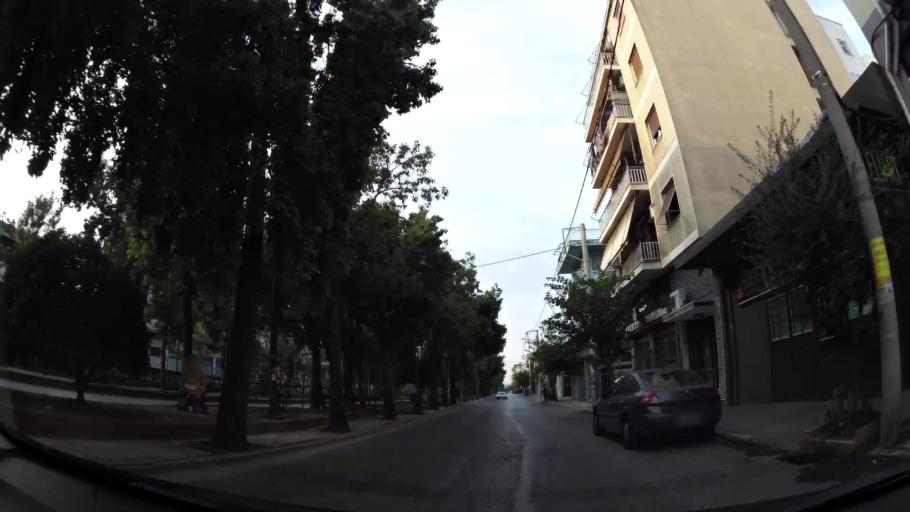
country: GR
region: Attica
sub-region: Nomarchia Athinas
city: Athens
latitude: 37.9828
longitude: 23.7130
